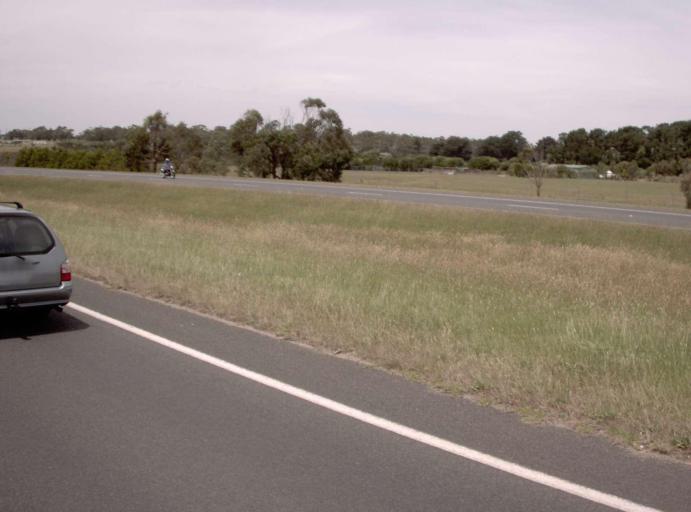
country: AU
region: Victoria
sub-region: Mornington Peninsula
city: Safety Beach
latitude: -38.3191
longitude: 145.0093
